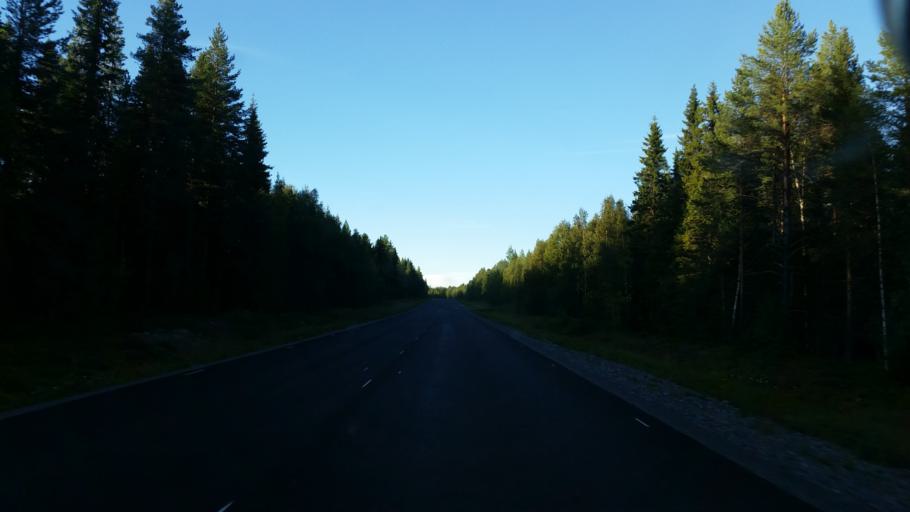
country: SE
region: Vaesterbotten
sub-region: Dorotea Kommun
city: Dorotea
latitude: 64.3053
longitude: 16.5938
